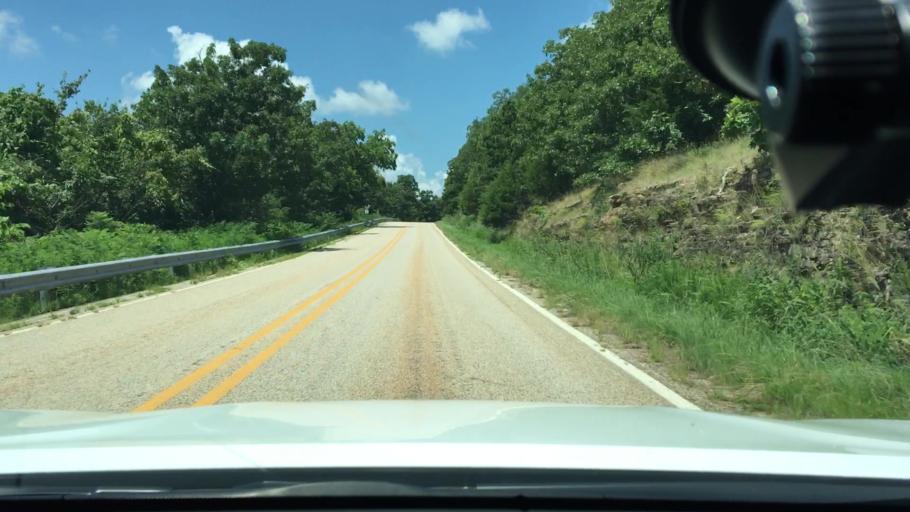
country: US
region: Arkansas
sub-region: Logan County
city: Paris
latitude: 35.1756
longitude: -93.5911
